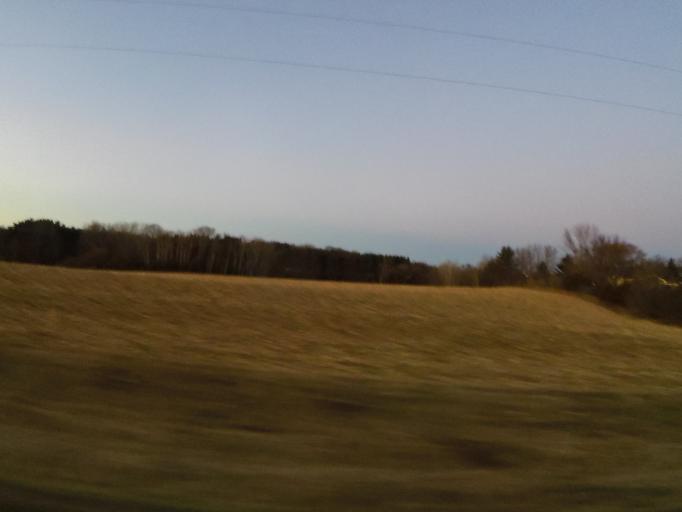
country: US
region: Wisconsin
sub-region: Pierce County
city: River Falls
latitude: 44.9314
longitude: -92.6710
